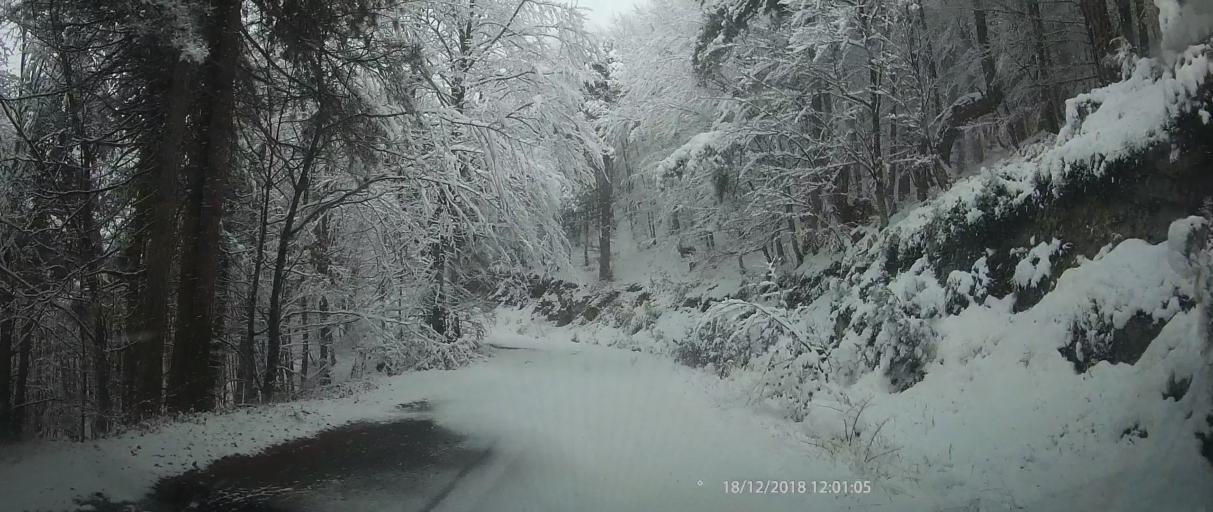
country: GR
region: Central Macedonia
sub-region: Nomos Pierias
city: Litochoro
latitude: 40.1095
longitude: 22.4624
